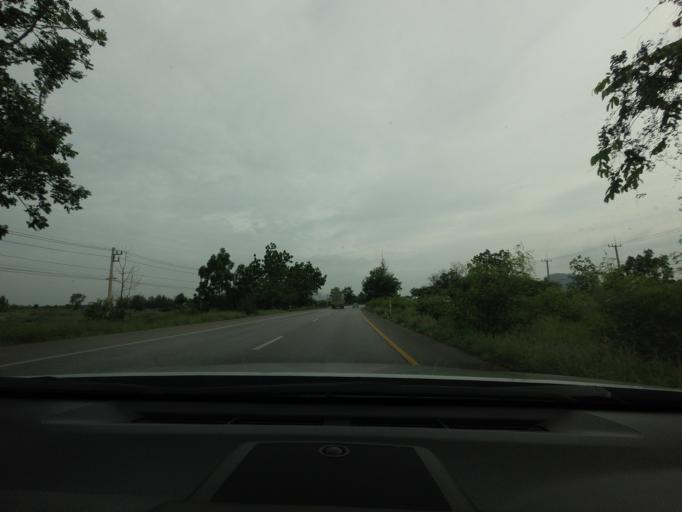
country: TH
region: Phetchaburi
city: Cha-am
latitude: 12.7290
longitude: 99.9269
